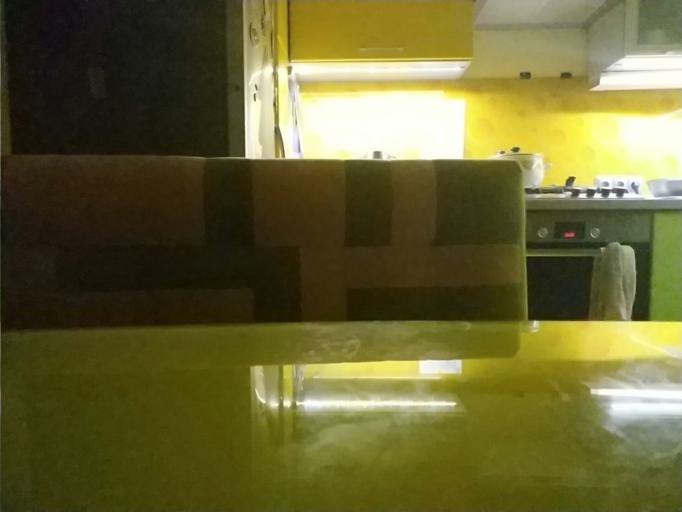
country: RU
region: Republic of Karelia
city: Pyaozerskiy
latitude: 65.6115
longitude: 30.5592
